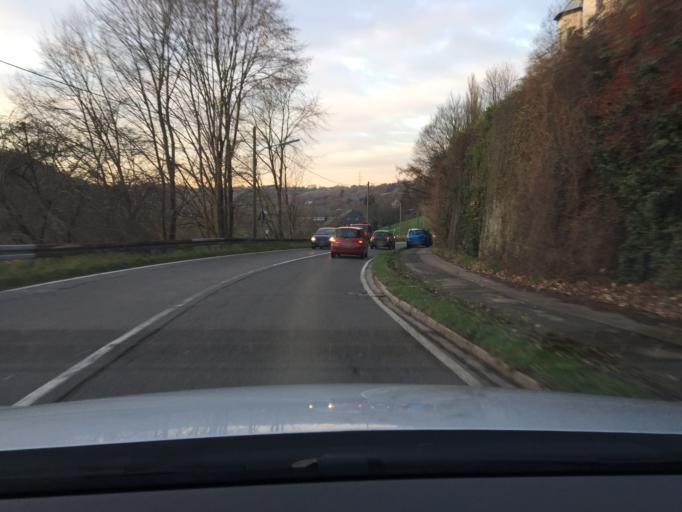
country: DE
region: North Rhine-Westphalia
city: Hattingen
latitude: 51.3766
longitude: 7.1280
